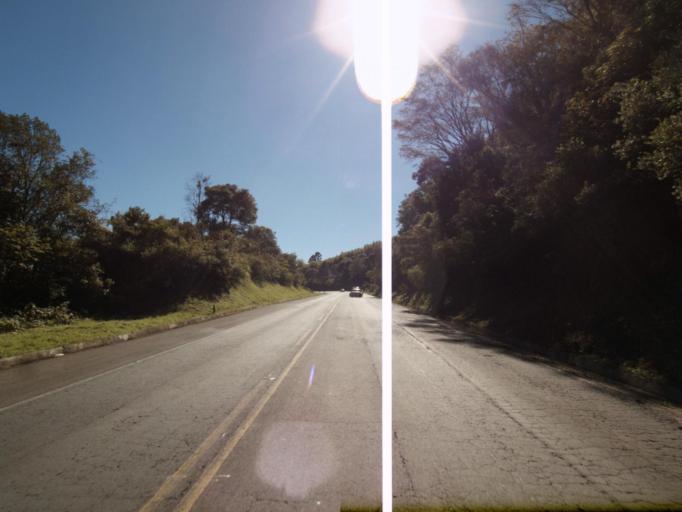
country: BR
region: Rio Grande do Sul
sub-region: Frederico Westphalen
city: Frederico Westphalen
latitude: -26.8425
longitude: -53.1716
